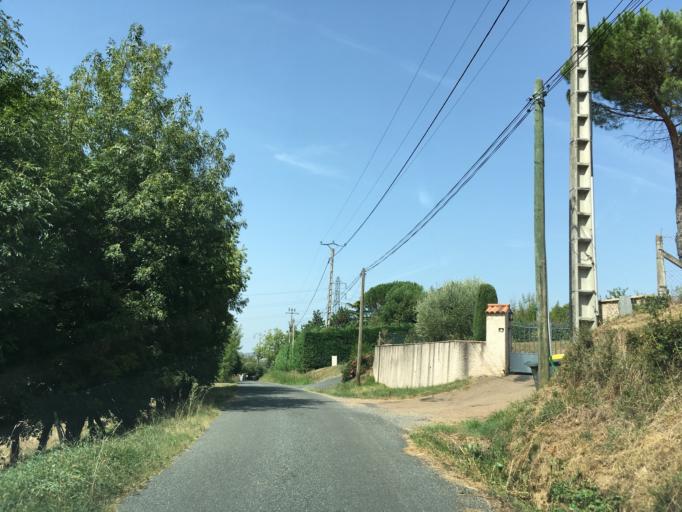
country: FR
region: Midi-Pyrenees
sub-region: Departement du Tarn
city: Lagarrigue
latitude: 43.6105
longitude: 2.2834
